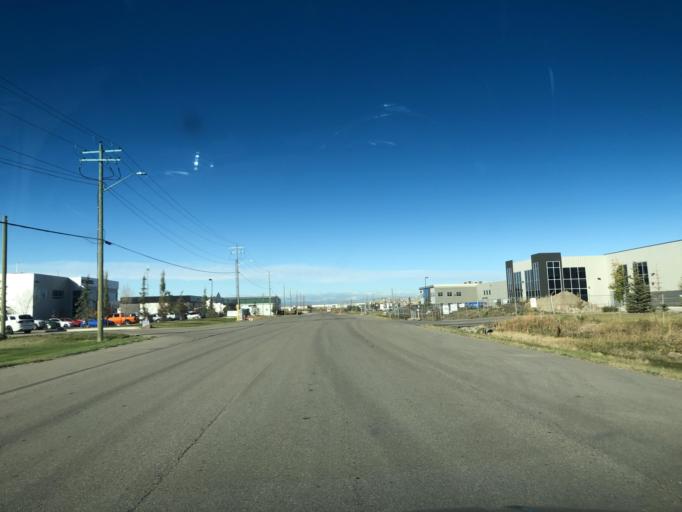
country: CA
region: Alberta
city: Chestermere
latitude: 50.9624
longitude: -113.9041
